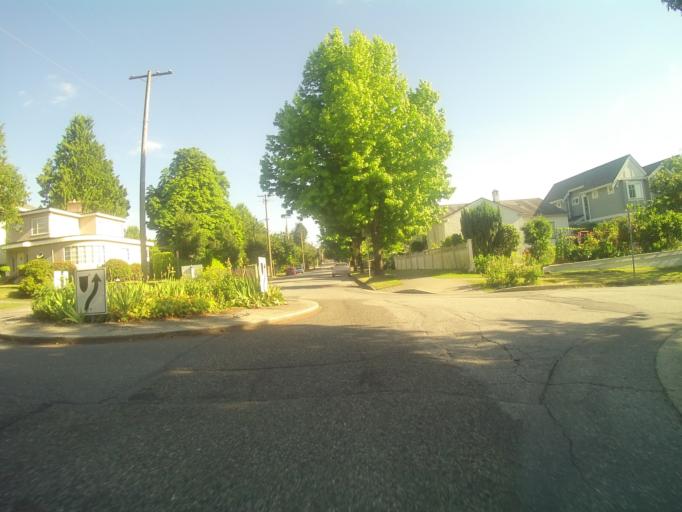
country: CA
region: British Columbia
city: Vancouver
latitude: 49.2472
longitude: -123.1205
